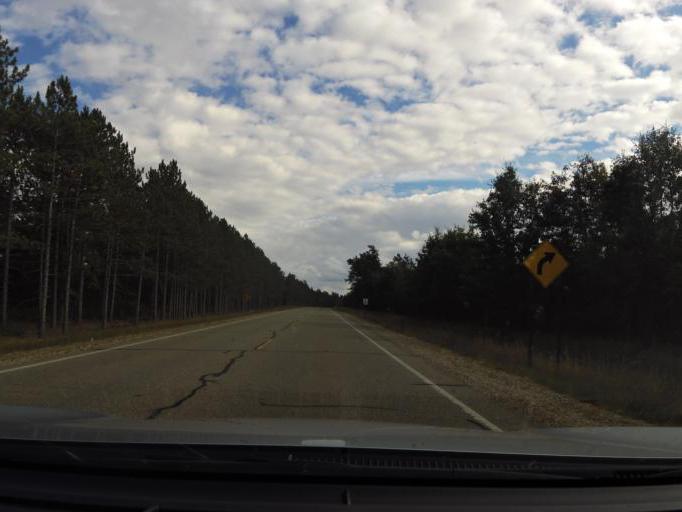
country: US
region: Michigan
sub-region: Roscommon County
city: Roscommon
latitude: 44.4632
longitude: -84.5328
